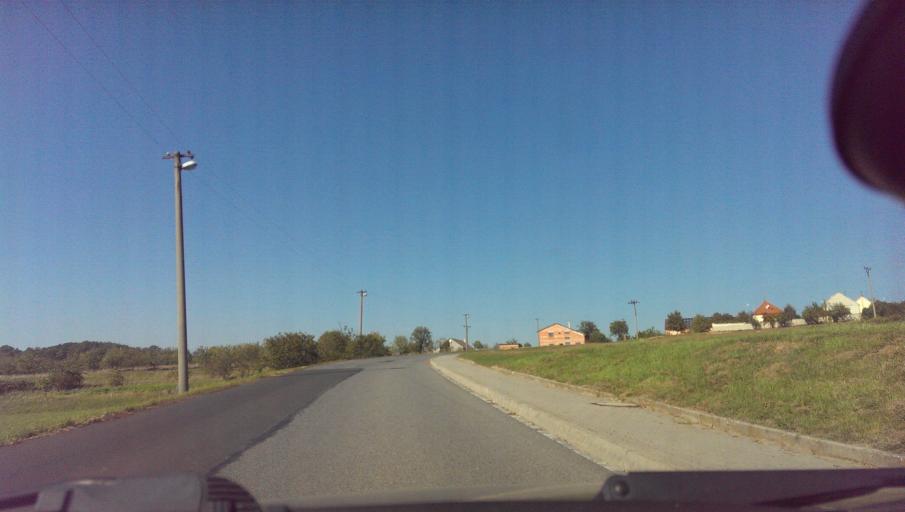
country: CZ
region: Zlin
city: Popovice
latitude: 49.0494
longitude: 17.5209
